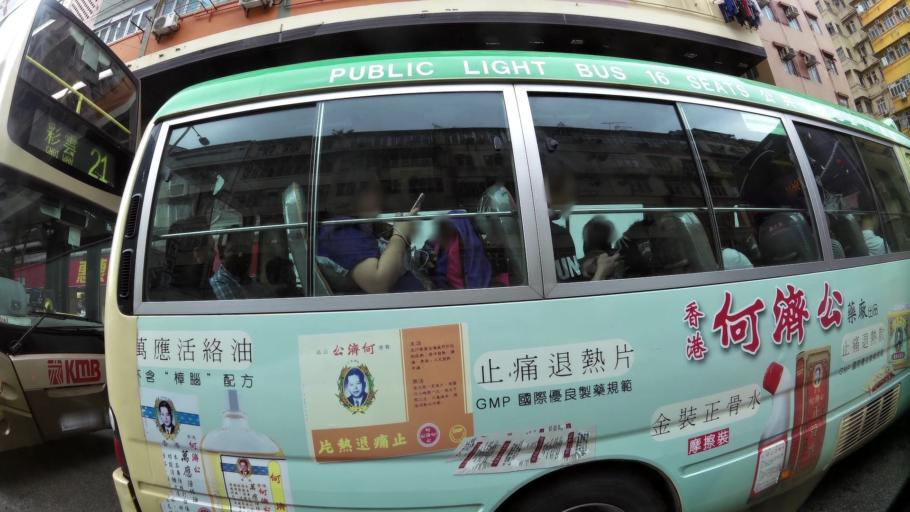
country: HK
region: Kowloon City
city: Kowloon
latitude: 22.3066
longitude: 114.1841
